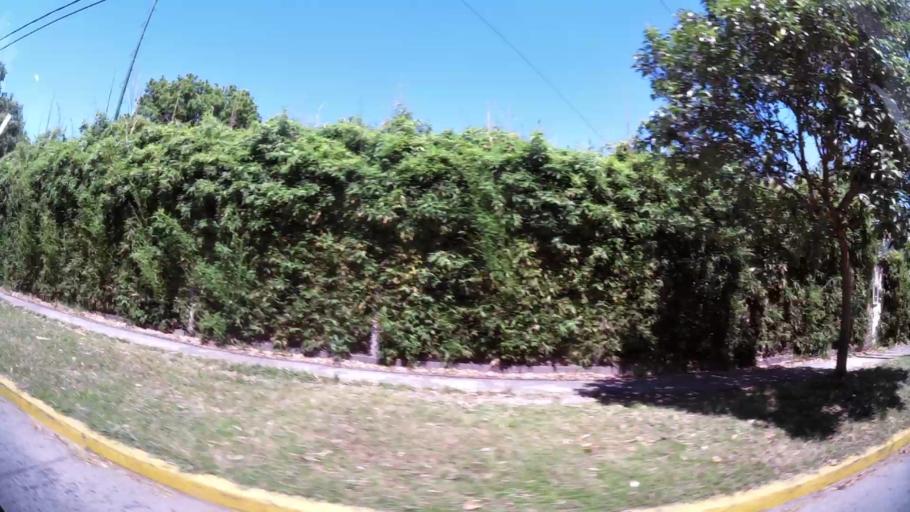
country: AR
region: Buenos Aires
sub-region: Partido de Tigre
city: Tigre
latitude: -34.4938
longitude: -58.6294
